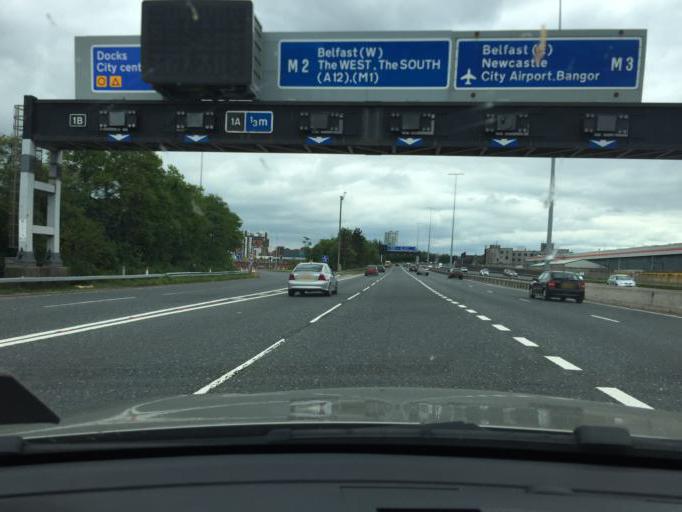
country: GB
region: Northern Ireland
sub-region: City of Belfast
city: Belfast
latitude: 54.6143
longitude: -5.9209
